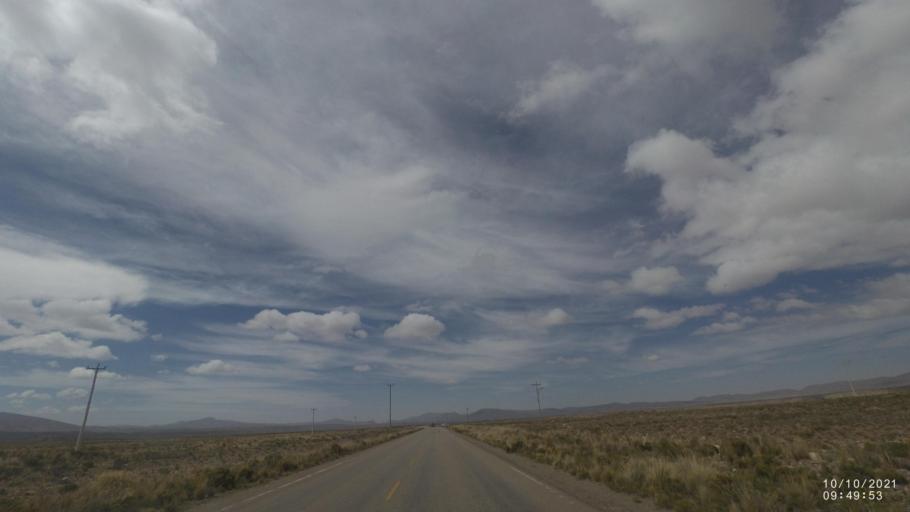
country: BO
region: La Paz
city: Colquiri
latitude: -17.2341
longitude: -67.3355
